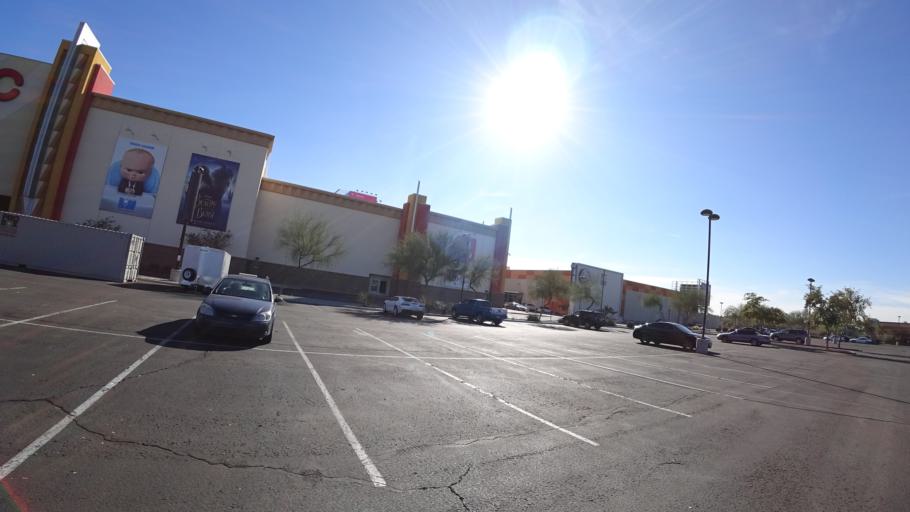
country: US
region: Arizona
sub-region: Maricopa County
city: Peoria
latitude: 33.5361
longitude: -112.2617
